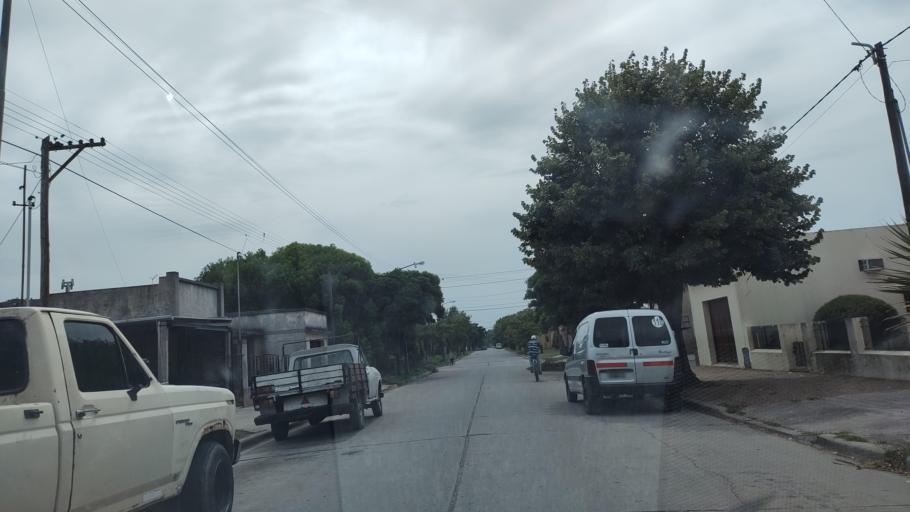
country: AR
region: Buenos Aires
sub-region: Partido de Loberia
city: Loberia
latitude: -38.1642
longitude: -58.7764
